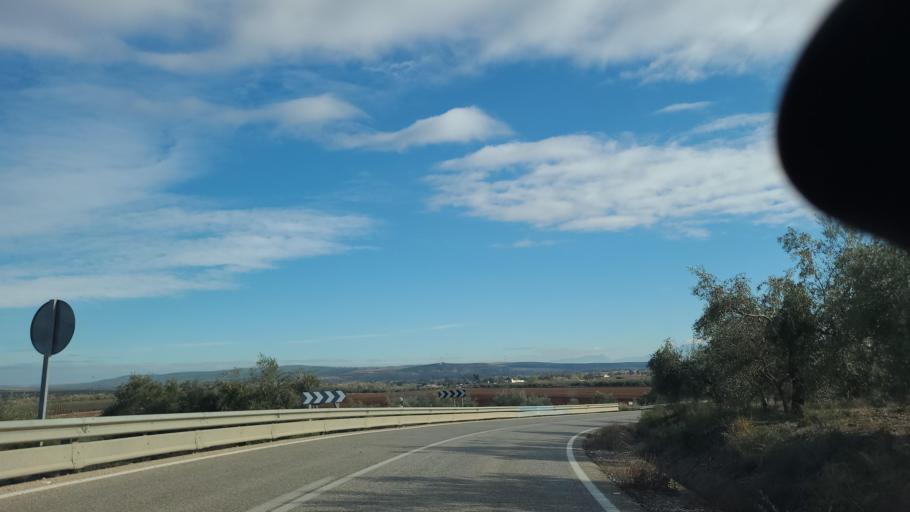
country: ES
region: Andalusia
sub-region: Provincia de Jaen
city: Espeluy
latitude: 38.0229
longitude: -3.8477
